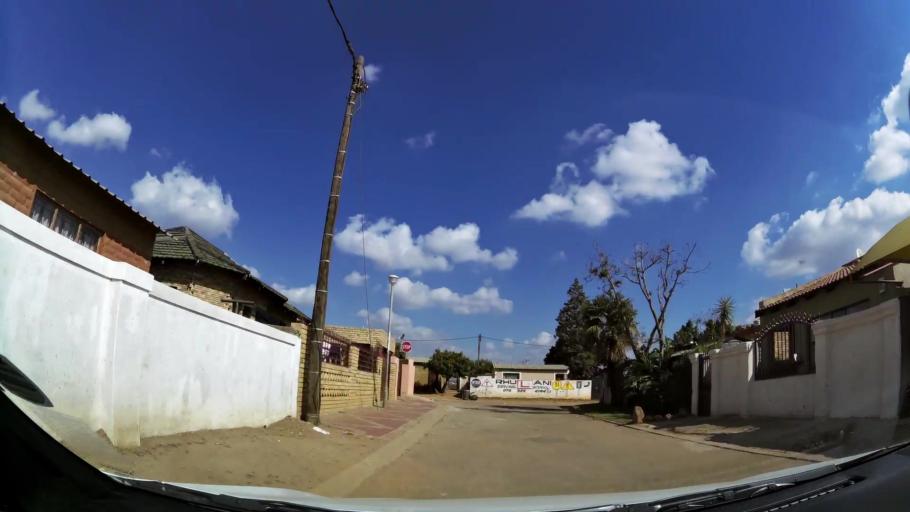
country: ZA
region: Gauteng
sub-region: City of Tshwane Metropolitan Municipality
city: Cullinan
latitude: -25.7101
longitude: 28.4098
